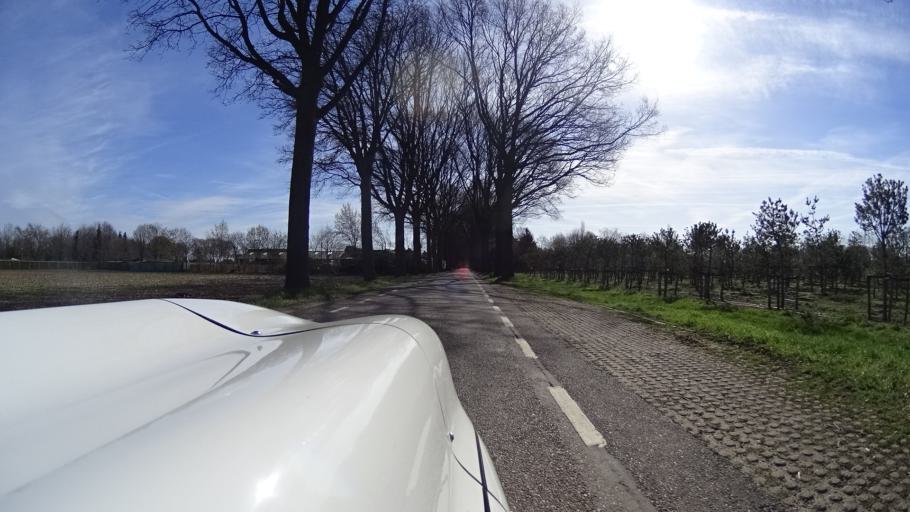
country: NL
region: North Brabant
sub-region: Gemeente Cuijk
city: Cuijk
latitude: 51.7141
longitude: 5.8401
